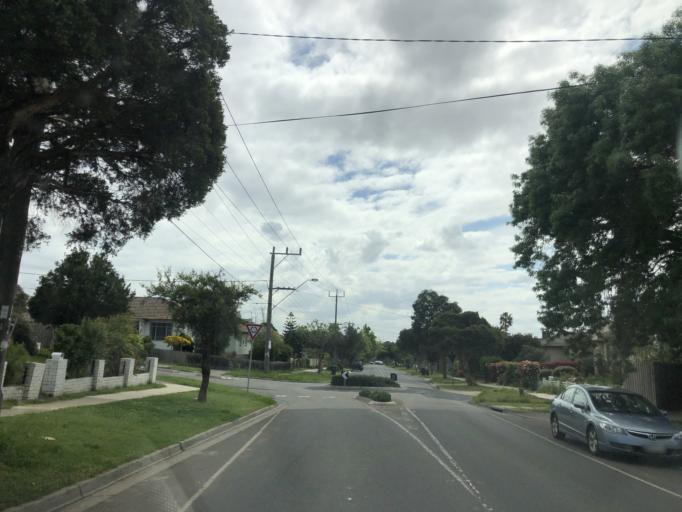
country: AU
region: Victoria
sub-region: Monash
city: Ashwood
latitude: -37.8793
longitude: 145.1057
